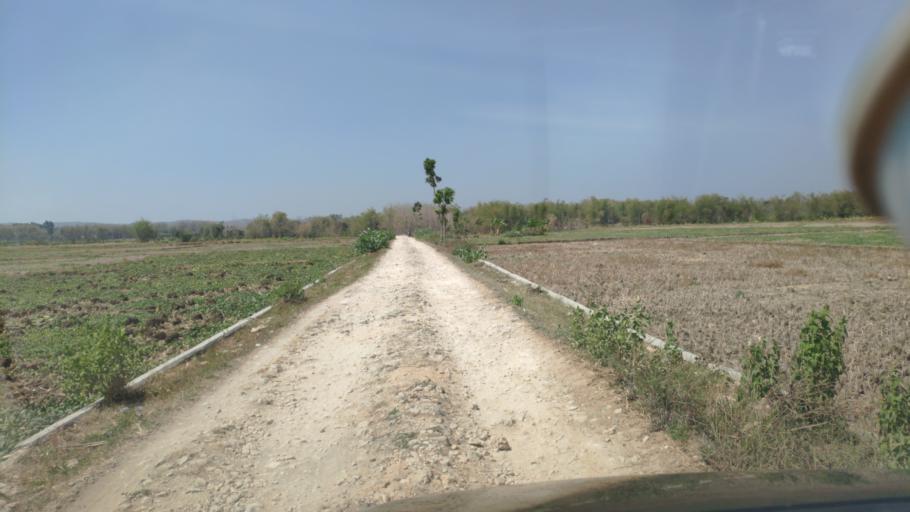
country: ID
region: Central Java
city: Mojo Wetan
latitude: -7.0312
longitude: 111.3609
